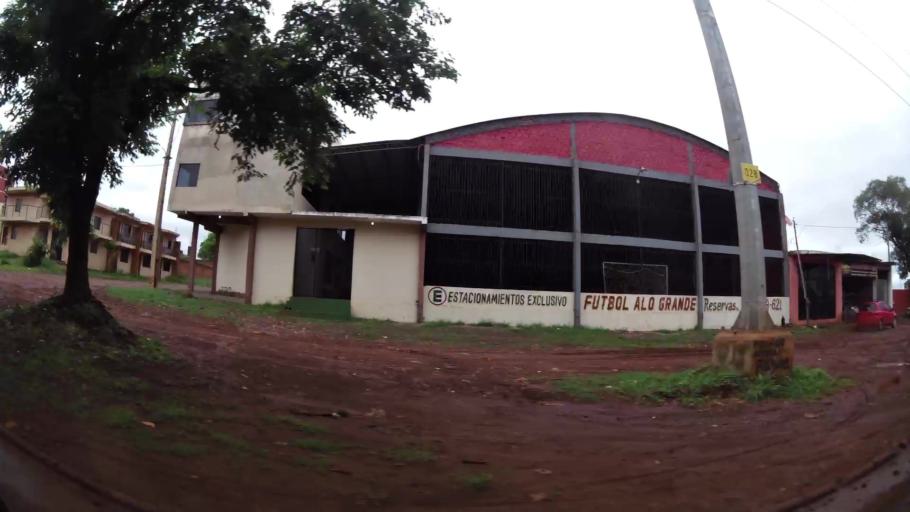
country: PY
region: Alto Parana
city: Presidente Franco
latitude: -25.5153
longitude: -54.6749
